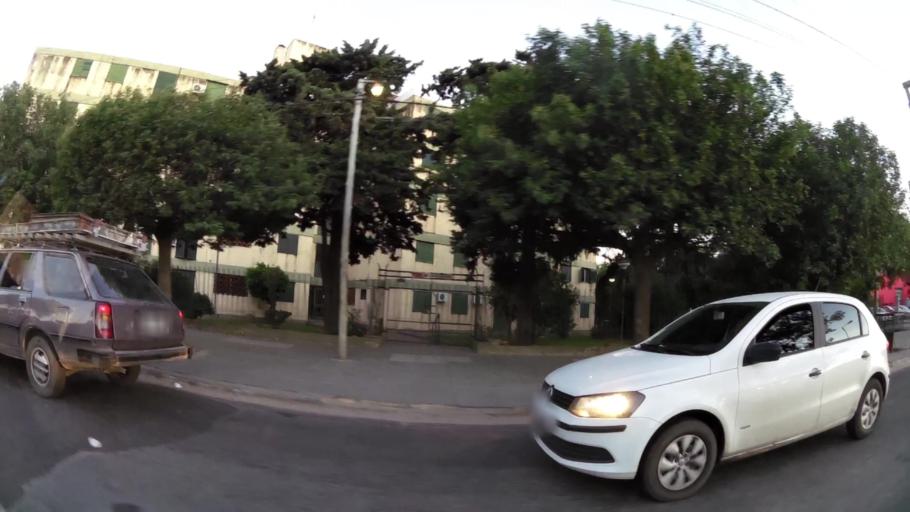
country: AR
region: Buenos Aires
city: San Justo
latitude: -34.7216
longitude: -58.5969
